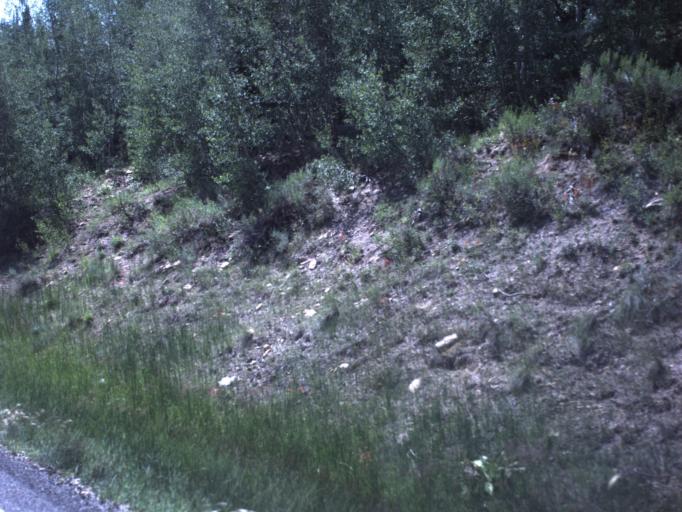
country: US
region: Utah
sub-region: Sanpete County
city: Fairview
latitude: 39.6496
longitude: -111.1536
